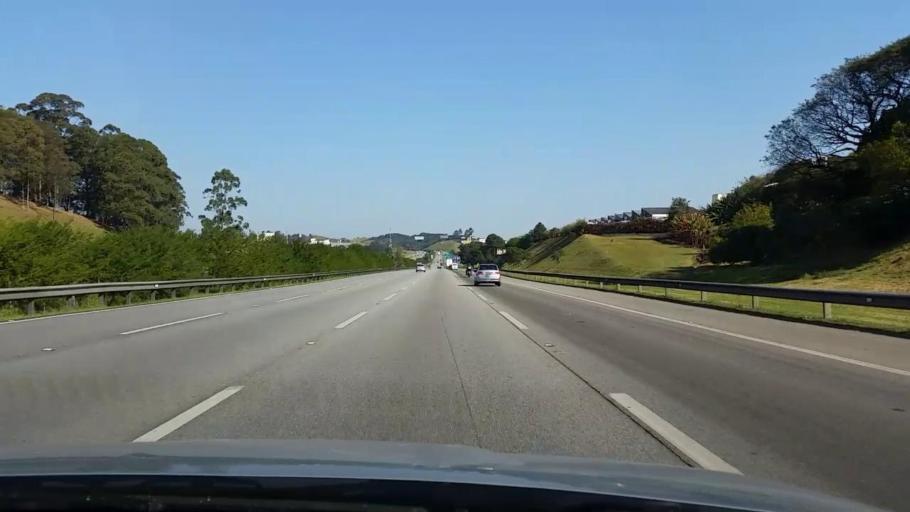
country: BR
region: Sao Paulo
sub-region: Diadema
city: Diadema
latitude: -23.7110
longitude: -46.6042
